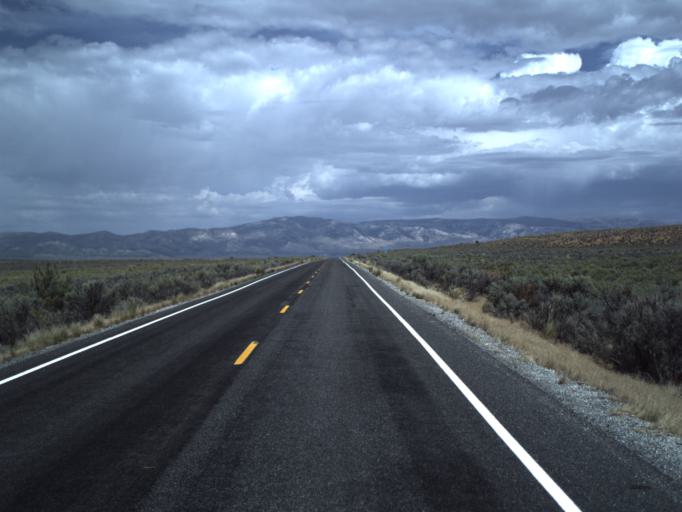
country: US
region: Idaho
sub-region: Cassia County
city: Burley
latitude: 41.6789
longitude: -113.5413
